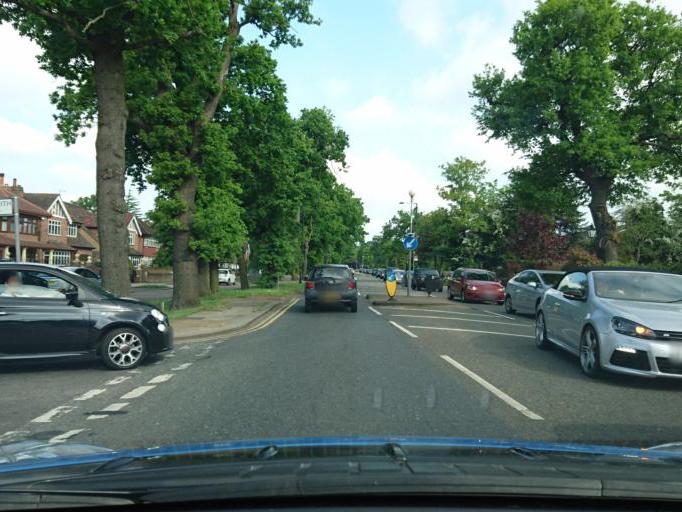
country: GB
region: England
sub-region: Greater London
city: Hadley Wood
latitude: 51.6383
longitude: -0.1409
